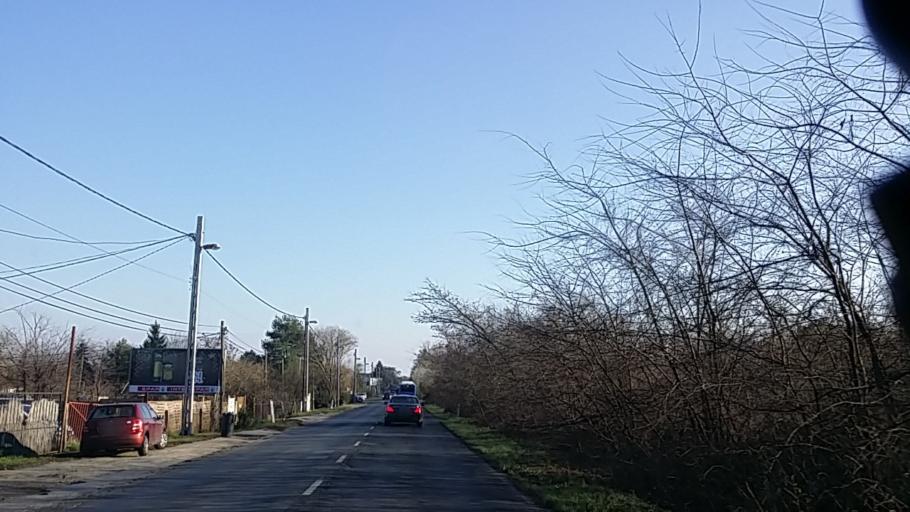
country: HU
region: Budapest
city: Budapest XVIII. keruelet
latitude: 47.4548
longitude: 19.2174
